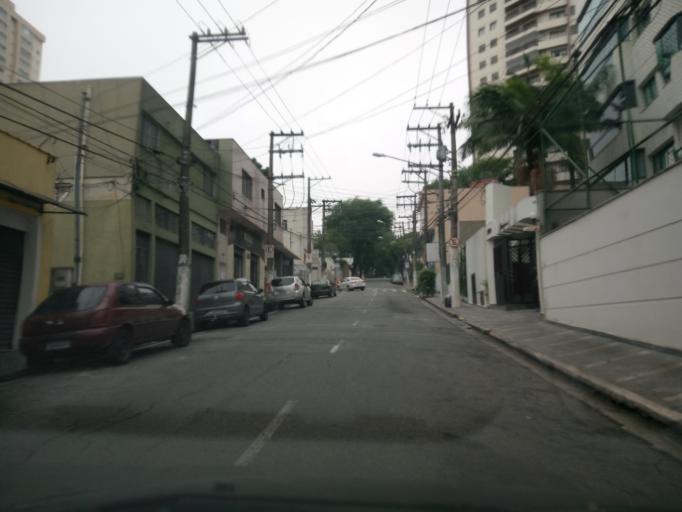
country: BR
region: Sao Paulo
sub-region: Sao Bernardo Do Campo
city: Sao Bernardo do Campo
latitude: -23.7141
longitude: -46.5466
